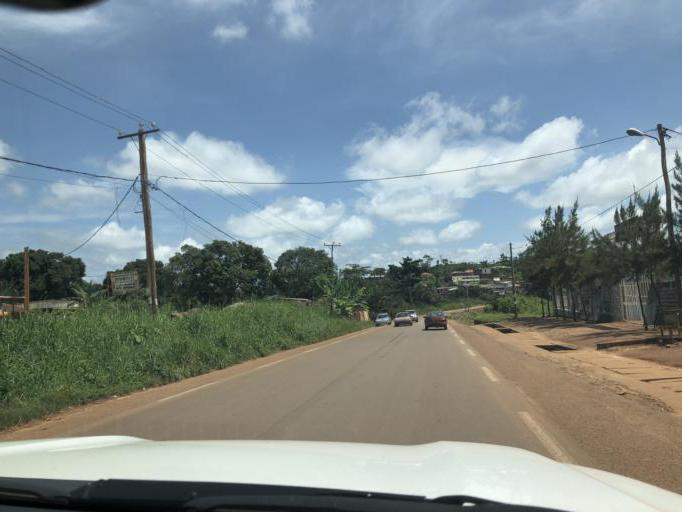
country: CM
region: Centre
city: Yaounde
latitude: 3.8642
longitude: 11.6155
